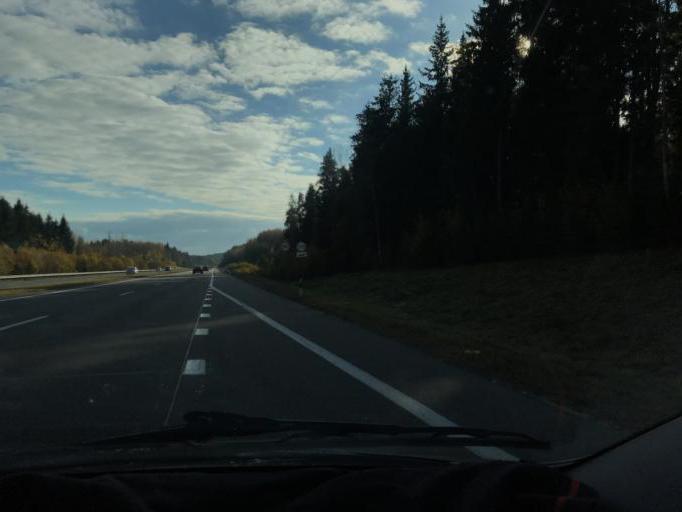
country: BY
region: Minsk
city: Lahoysk
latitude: 54.1313
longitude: 27.8081
